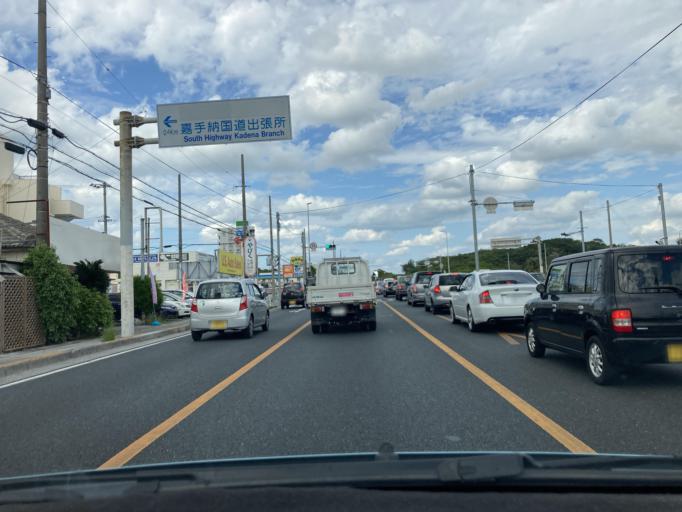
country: JP
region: Okinawa
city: Chatan
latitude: 26.3303
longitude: 127.7517
